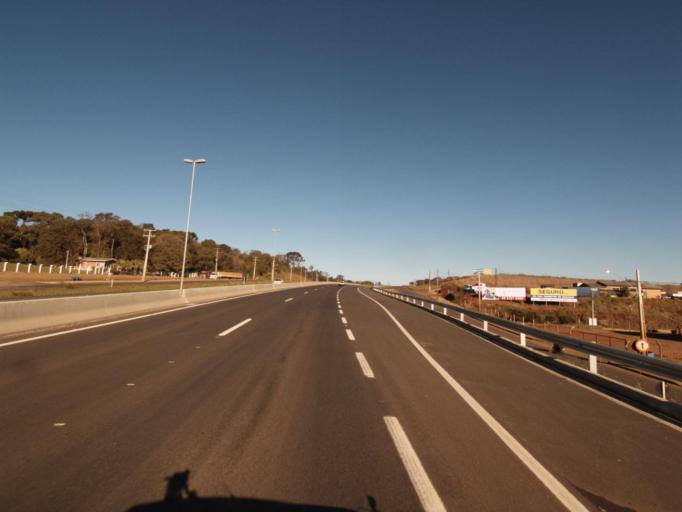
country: BR
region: Santa Catarina
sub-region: Chapeco
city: Chapeco
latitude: -27.0112
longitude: -52.6399
